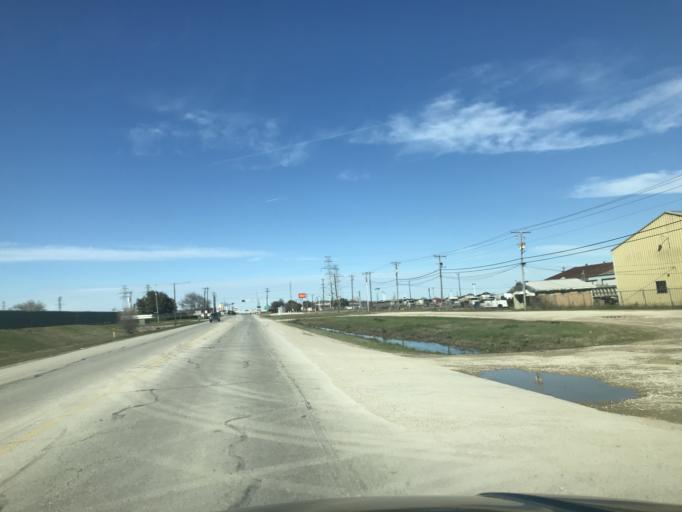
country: US
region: Texas
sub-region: Tarrant County
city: Blue Mound
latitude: 32.8348
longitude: -97.3429
